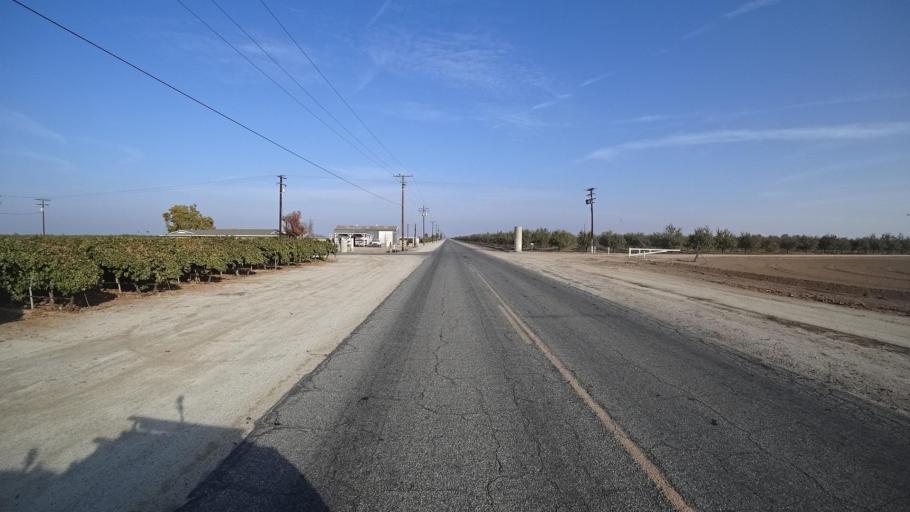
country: US
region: California
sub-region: Kern County
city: McFarland
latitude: 35.6815
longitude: -119.2048
